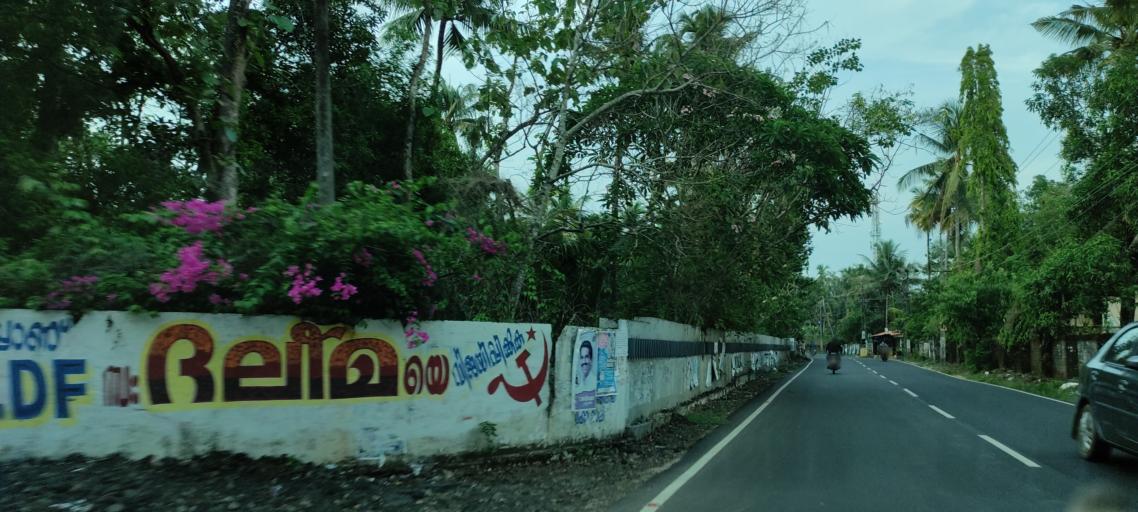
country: IN
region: Kerala
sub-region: Alappuzha
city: Kutiatodu
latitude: 9.7906
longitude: 76.3590
